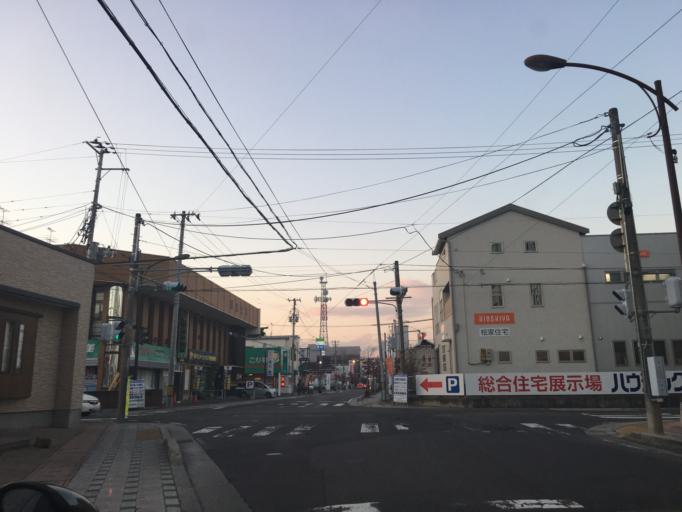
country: JP
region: Fukushima
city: Koriyama
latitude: 37.4053
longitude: 140.3574
